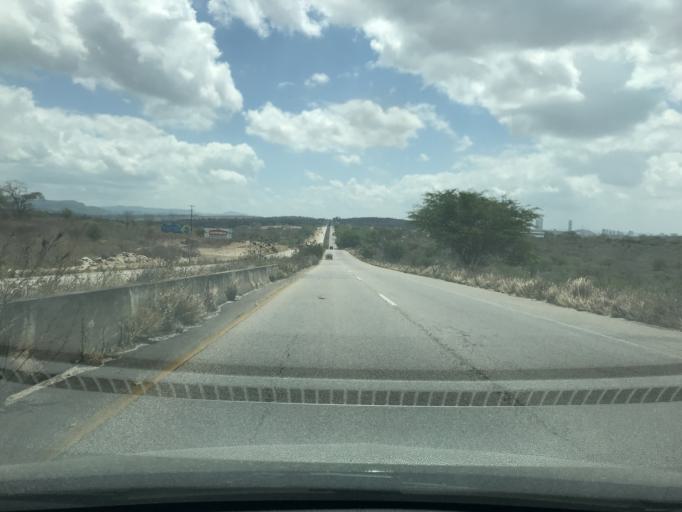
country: BR
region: Pernambuco
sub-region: Caruaru
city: Caruaru
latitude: -8.2992
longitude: -35.9061
